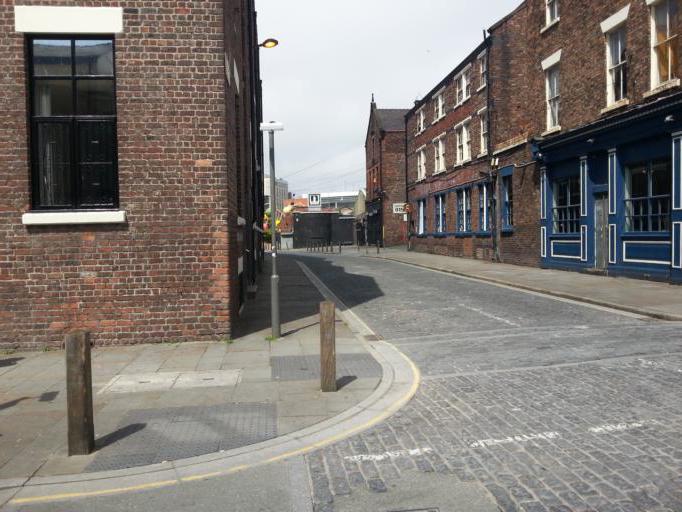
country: GB
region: England
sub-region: Liverpool
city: Liverpool
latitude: 53.4018
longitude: -2.9803
